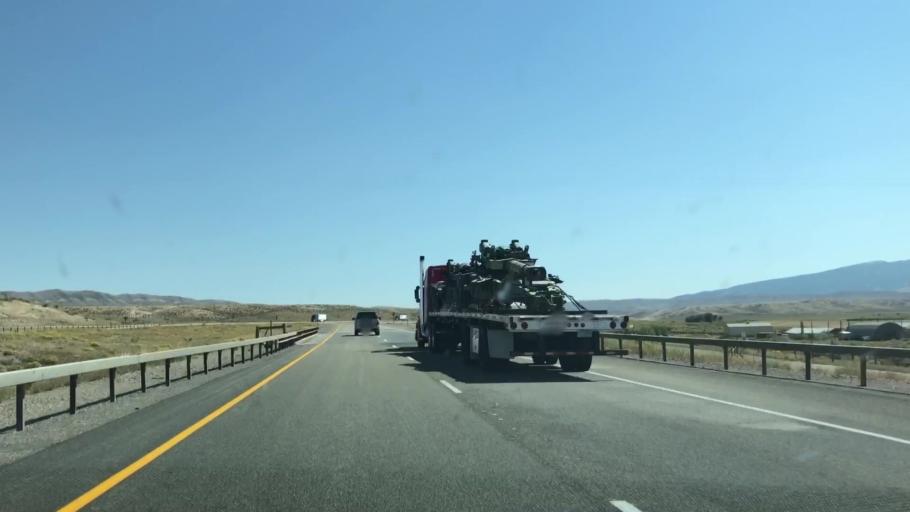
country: US
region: Wyoming
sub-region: Carbon County
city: Saratoga
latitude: 41.7419
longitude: -106.7796
